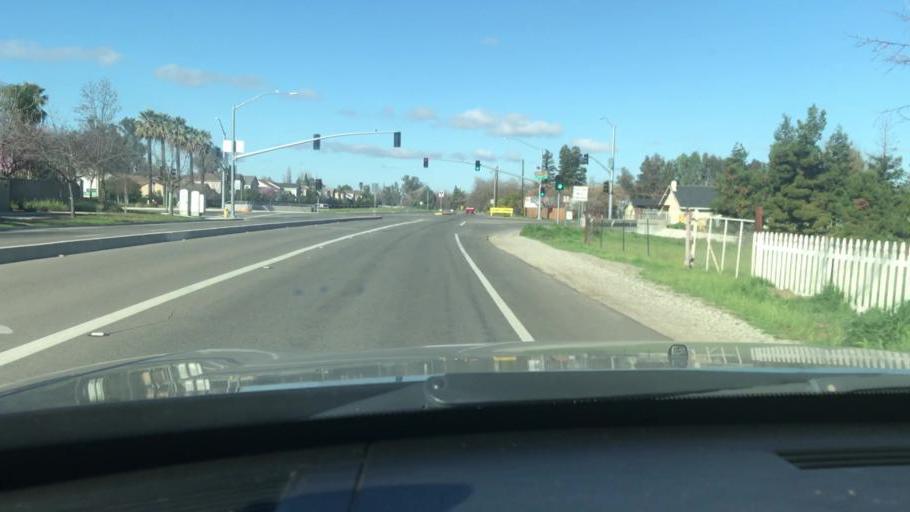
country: US
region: California
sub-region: Fresno County
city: Clovis
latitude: 36.8665
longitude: -119.6830
